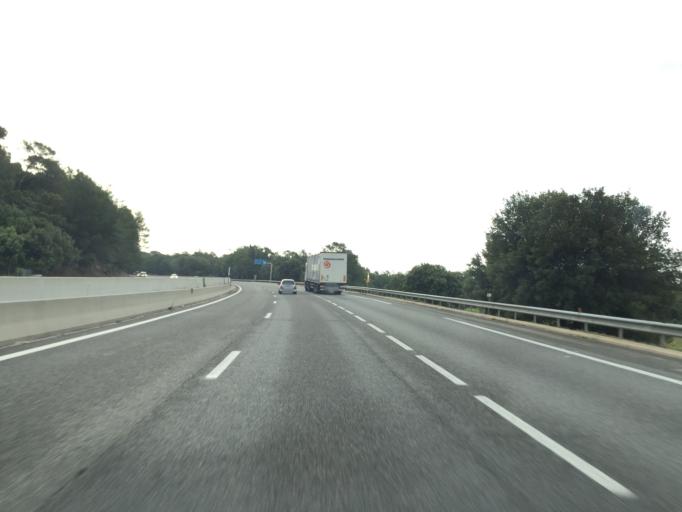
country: FR
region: Provence-Alpes-Cote d'Azur
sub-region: Departement du Var
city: Cabasse
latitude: 43.4051
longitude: 6.1947
